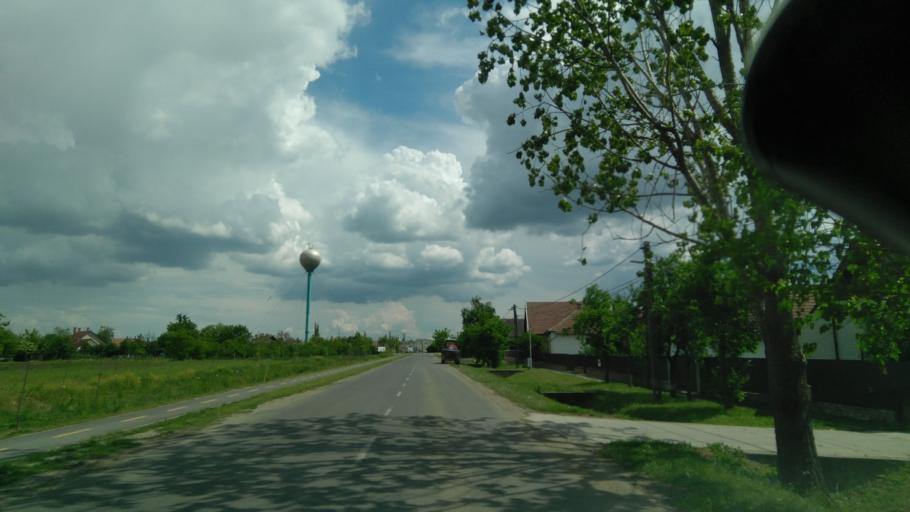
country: HU
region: Bekes
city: Korosladany
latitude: 46.9677
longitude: 21.0698
